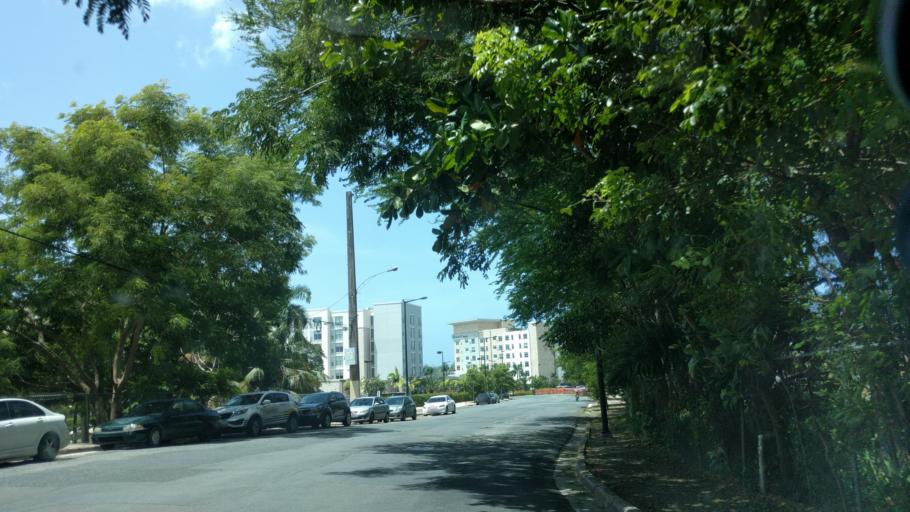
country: PR
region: San Juan
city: San Juan
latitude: 18.4542
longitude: -66.0874
